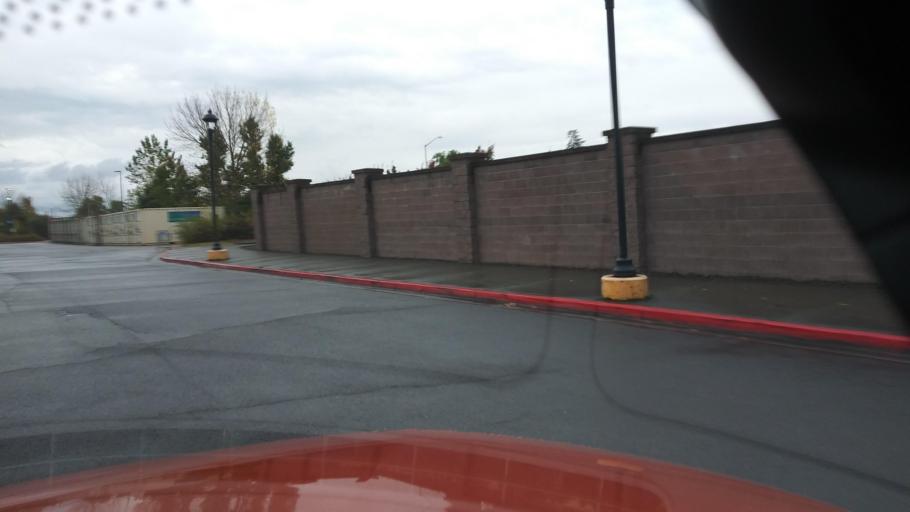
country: US
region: Oregon
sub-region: Washington County
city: Cornelius
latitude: 45.5214
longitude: -123.0703
